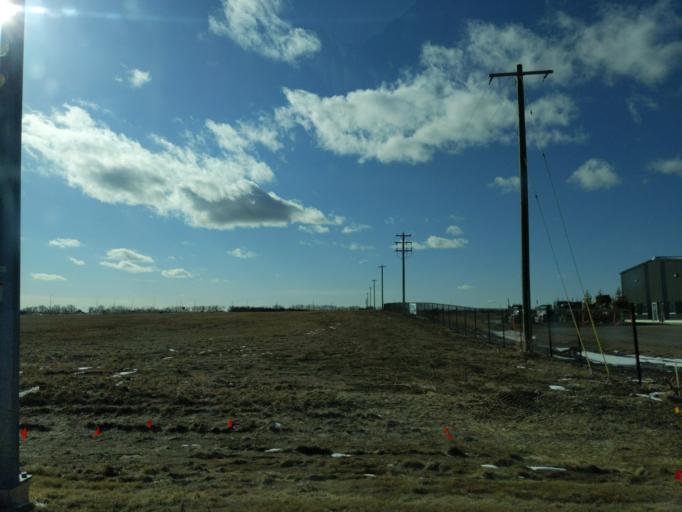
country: CA
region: Saskatchewan
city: Lloydminster
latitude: 53.3014
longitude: -110.0447
